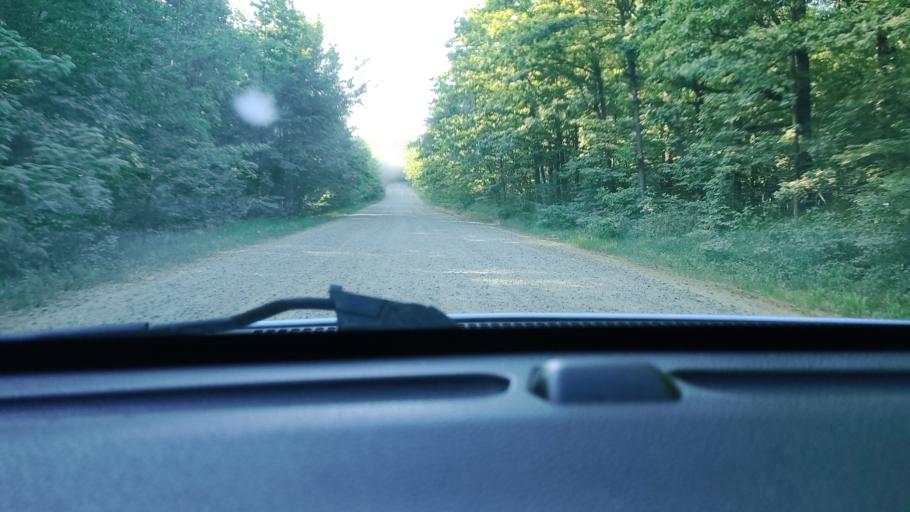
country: RU
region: Krasnodarskiy
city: Goryachiy Klyuch
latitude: 44.7103
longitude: 38.9923
